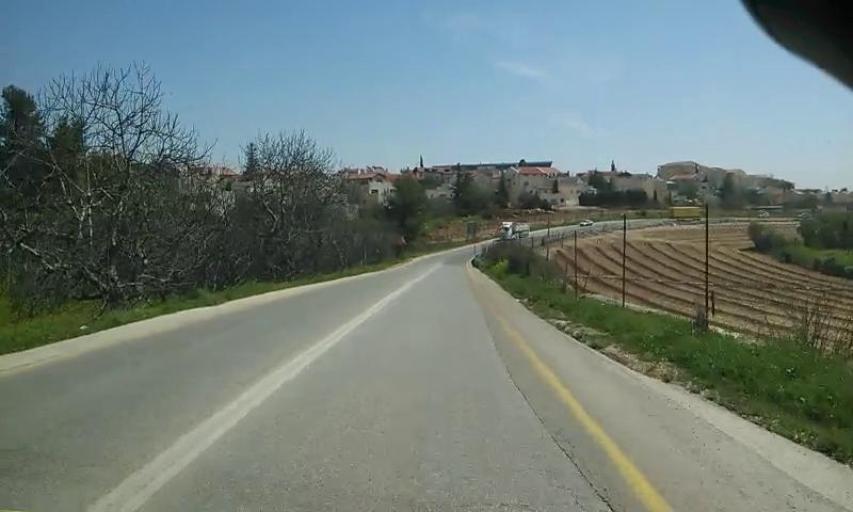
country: PS
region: West Bank
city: Nahhalin
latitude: 31.6540
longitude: 35.1237
